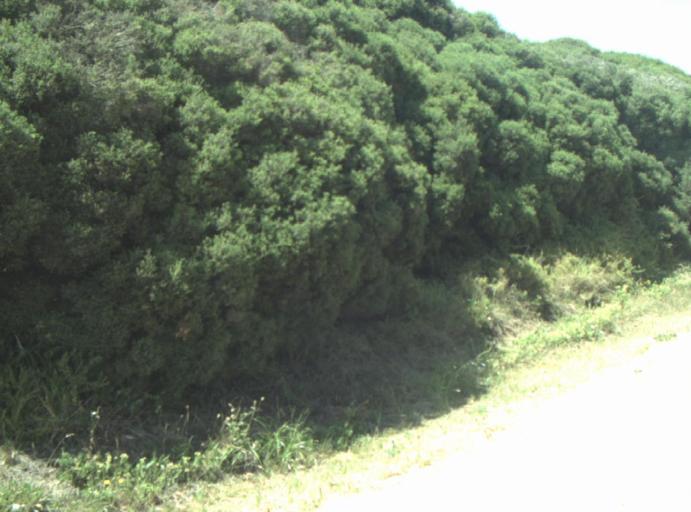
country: AU
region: Victoria
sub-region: Greater Geelong
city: Breakwater
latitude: -38.2748
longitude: 144.4027
